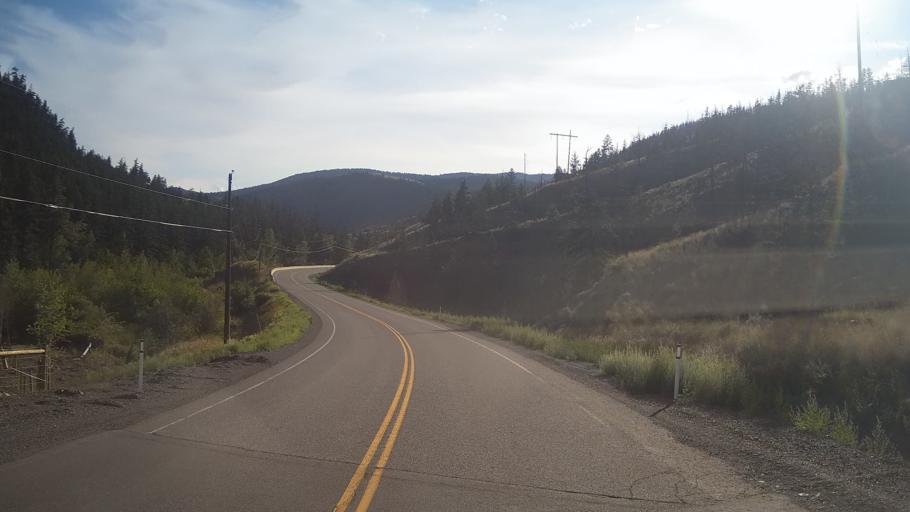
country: CA
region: British Columbia
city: Cache Creek
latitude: 50.8844
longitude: -121.4957
